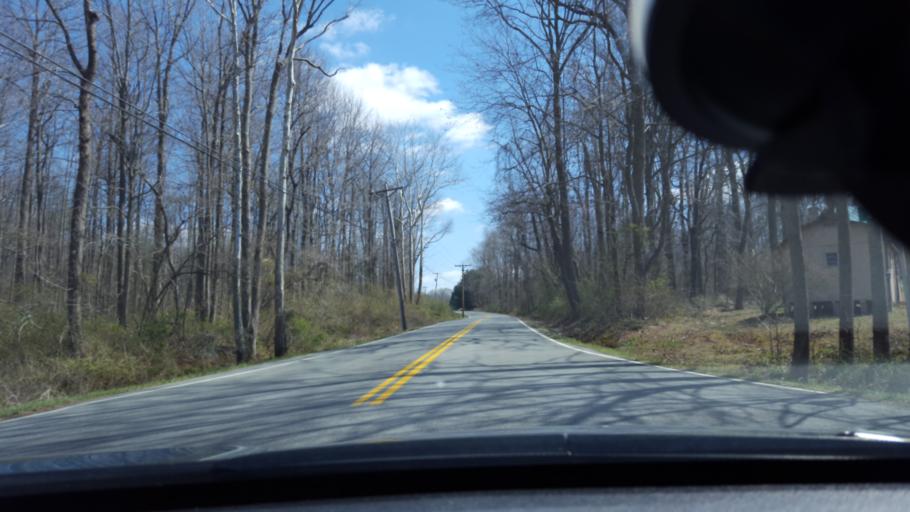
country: US
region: Maryland
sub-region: Calvert County
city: Huntingtown
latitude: 38.6255
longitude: -76.5773
